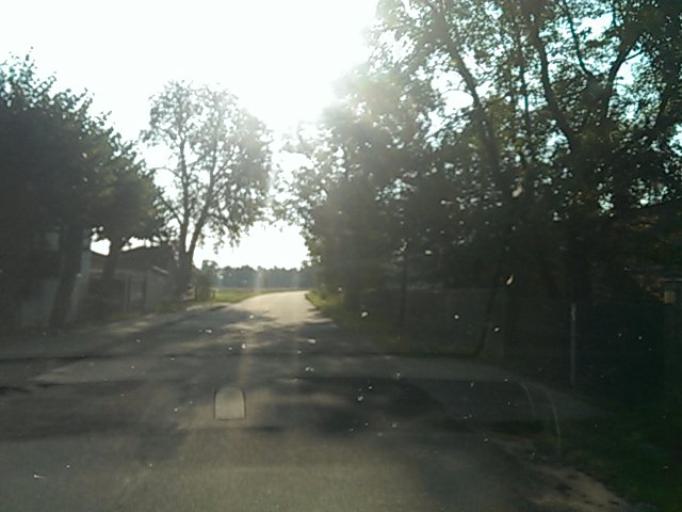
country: DE
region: Brandenburg
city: Michendorf
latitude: 52.2691
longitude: 13.1233
